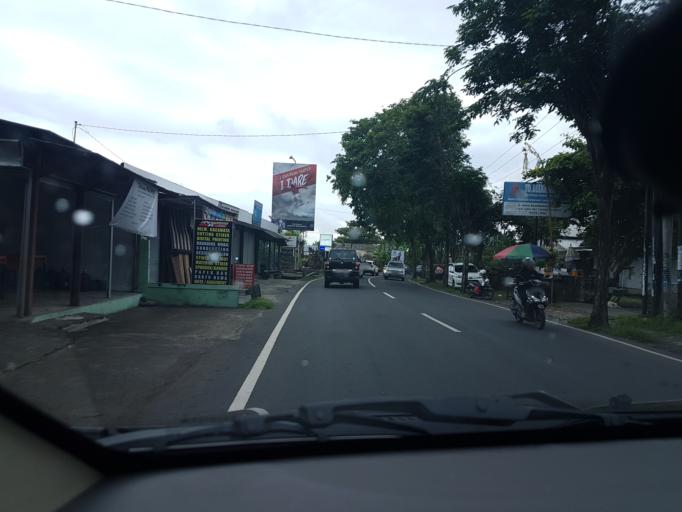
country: ID
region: Bali
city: Denpasar
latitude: -8.6643
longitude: 115.1674
